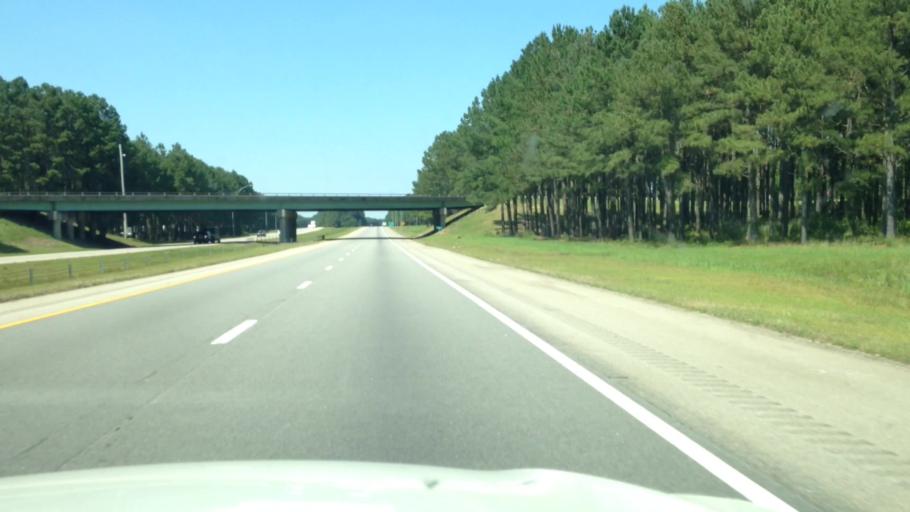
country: US
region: North Carolina
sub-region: Wilson County
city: Lucama
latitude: 35.7017
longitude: -78.0465
